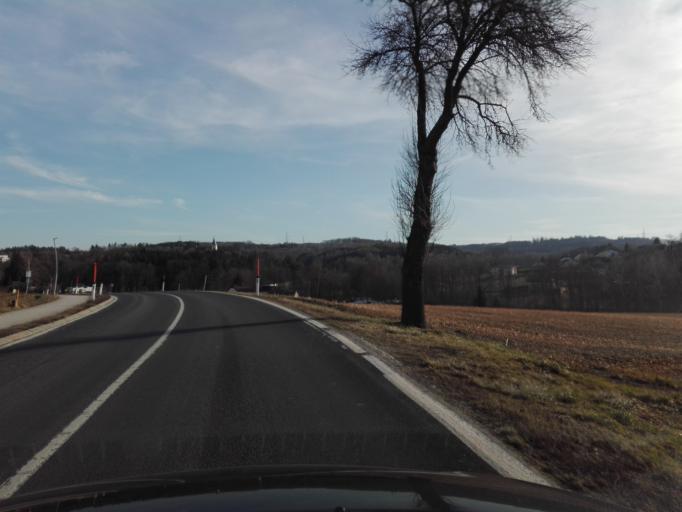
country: AT
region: Lower Austria
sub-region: Politischer Bezirk Amstetten
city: Amstetten
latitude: 48.1666
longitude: 14.8400
